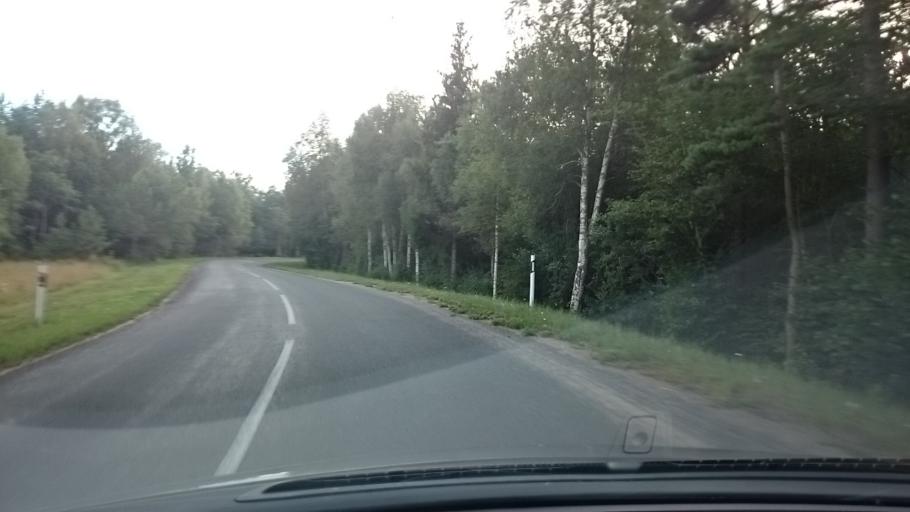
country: EE
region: Saare
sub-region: Kuressaare linn
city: Kuressaare
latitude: 58.4194
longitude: 22.1225
